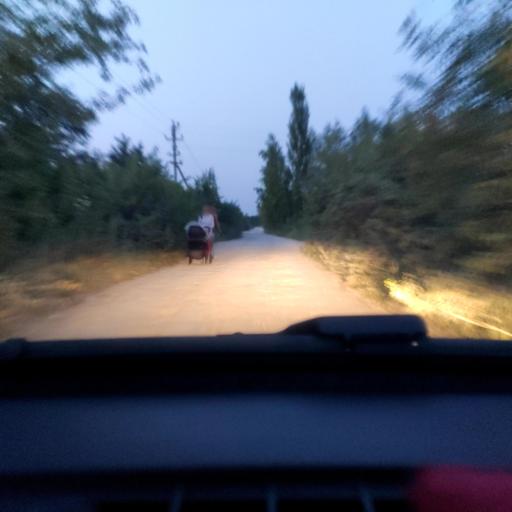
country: RU
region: Voronezj
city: Podgornoye
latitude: 51.8604
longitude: 39.1068
